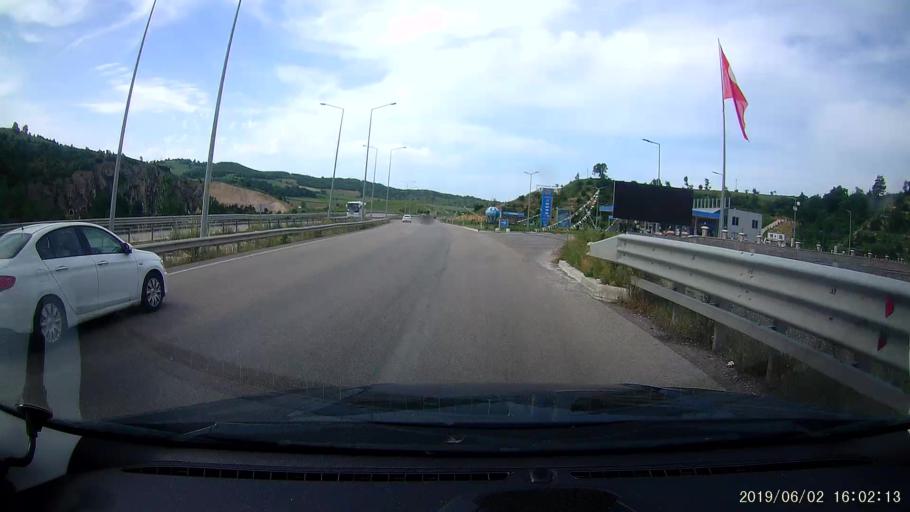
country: TR
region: Samsun
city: Havza
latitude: 40.9411
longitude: 35.6587
